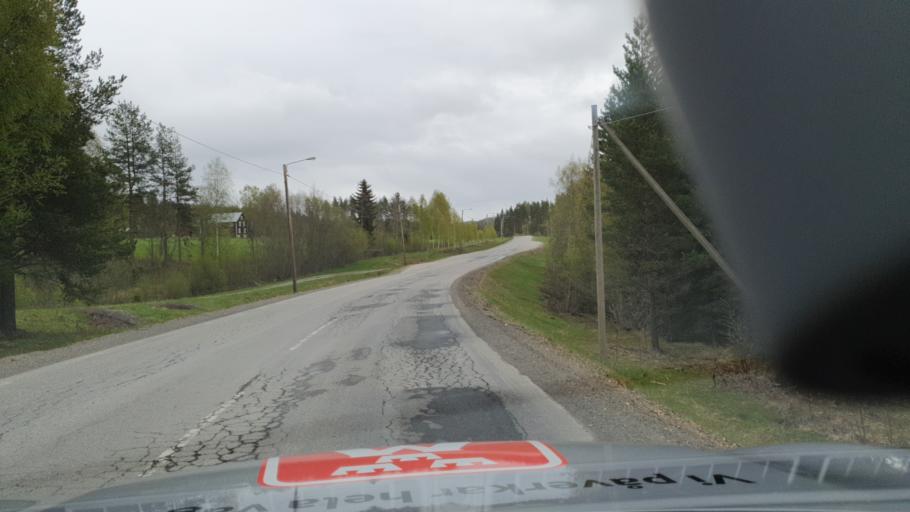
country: SE
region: Vaesternorrland
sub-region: OErnskoeldsviks Kommun
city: Bredbyn
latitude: 63.5098
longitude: 17.8060
